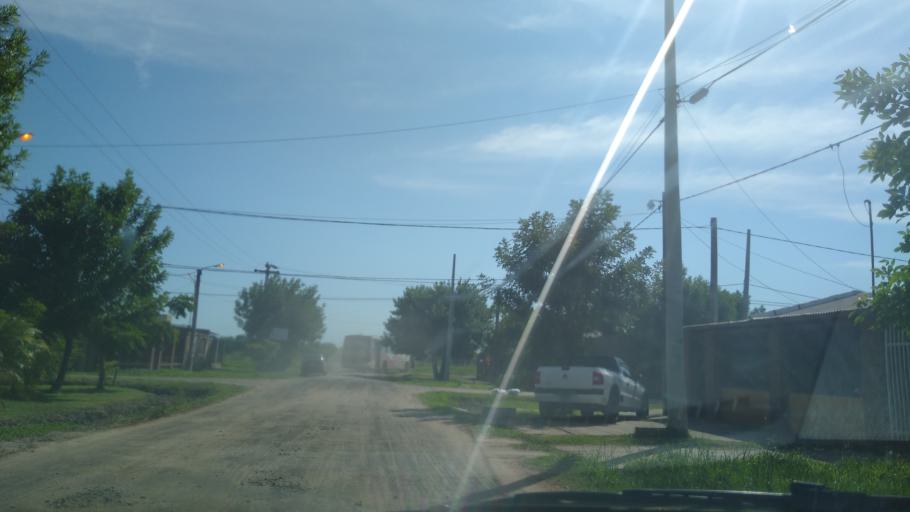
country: AR
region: Chaco
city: Barranqueras
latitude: -27.4930
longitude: -58.9579
